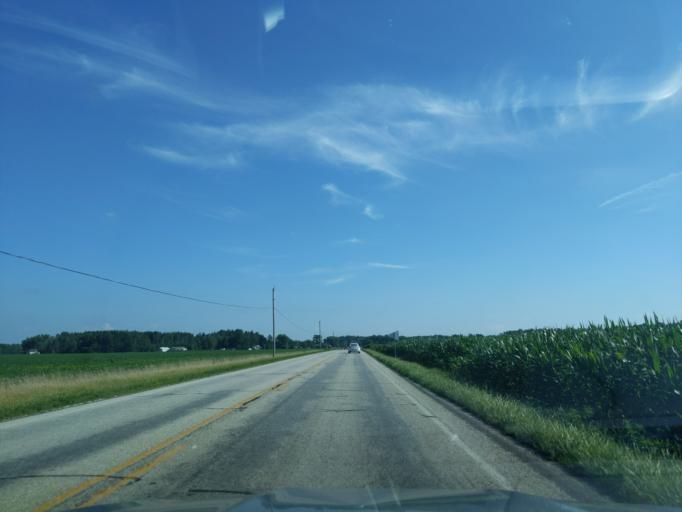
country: US
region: Indiana
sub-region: Ripley County
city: Osgood
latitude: 39.1127
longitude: -85.2801
